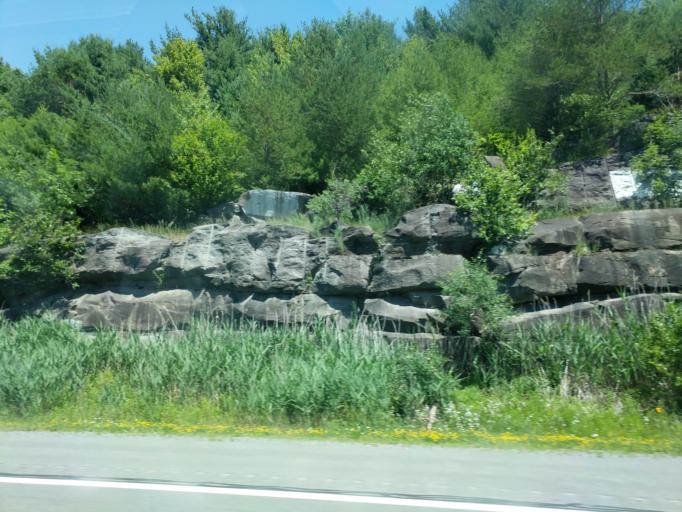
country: US
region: New York
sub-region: Sullivan County
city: Rock Hill
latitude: 41.6321
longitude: -74.6121
